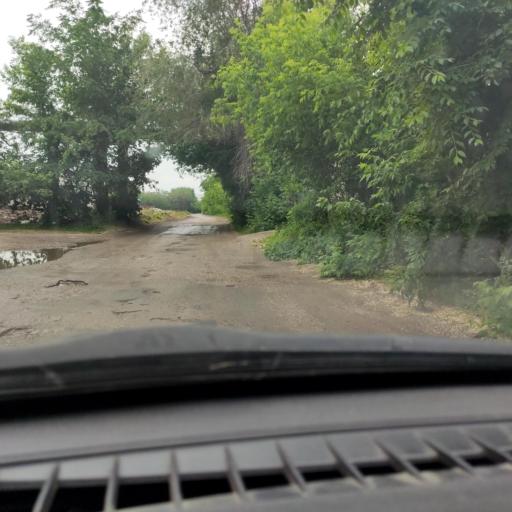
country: RU
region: Samara
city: Tol'yatti
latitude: 53.5203
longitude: 49.4541
